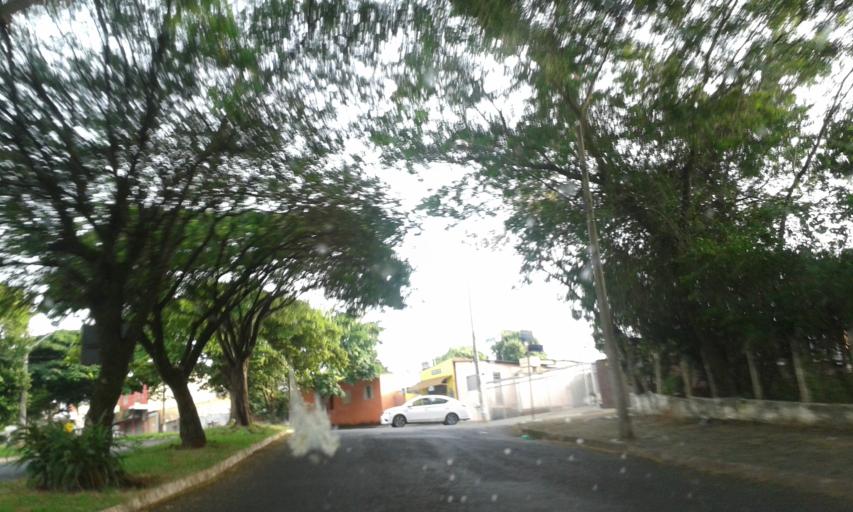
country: BR
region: Minas Gerais
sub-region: Uberlandia
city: Uberlandia
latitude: -18.9081
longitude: -48.2460
